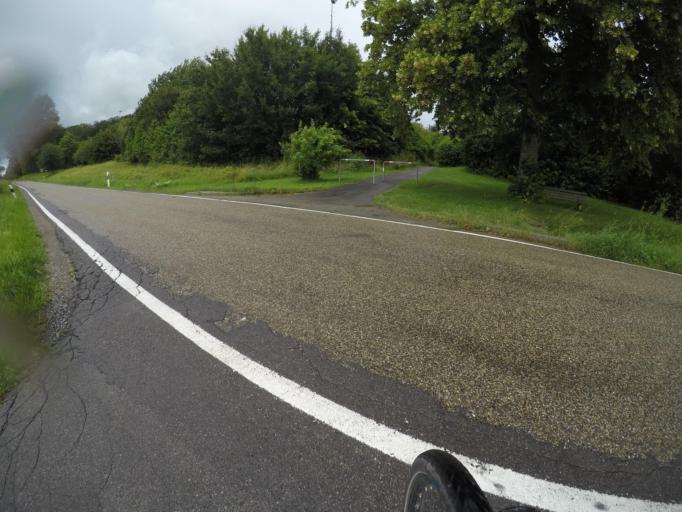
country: DE
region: Baden-Wuerttemberg
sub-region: Regierungsbezirk Stuttgart
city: Unterjettingen
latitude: 48.5662
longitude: 8.8296
